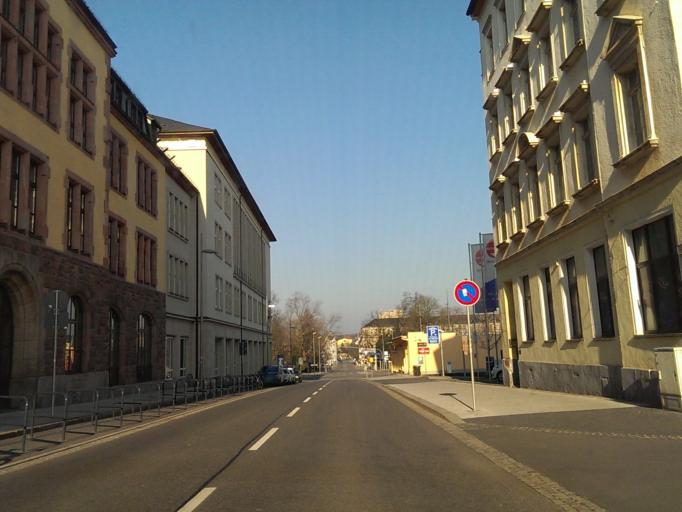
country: DE
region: Saxony
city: Chemnitz
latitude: 50.8396
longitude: 12.9293
